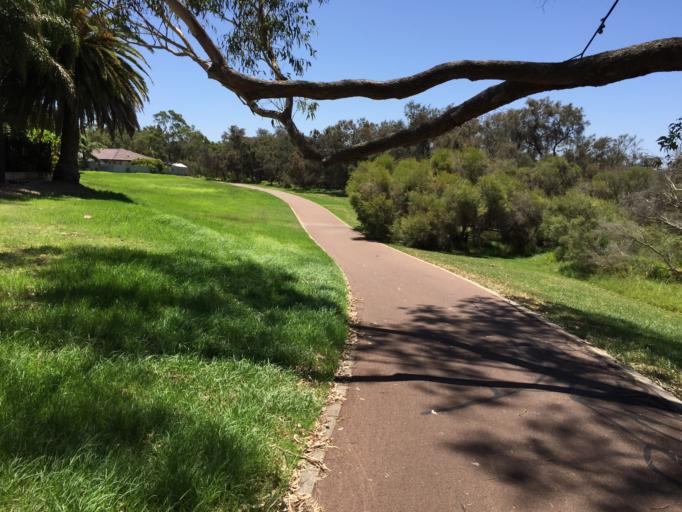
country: AU
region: Western Australia
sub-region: Canning
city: Wilson
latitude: -32.0323
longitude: 115.9045
